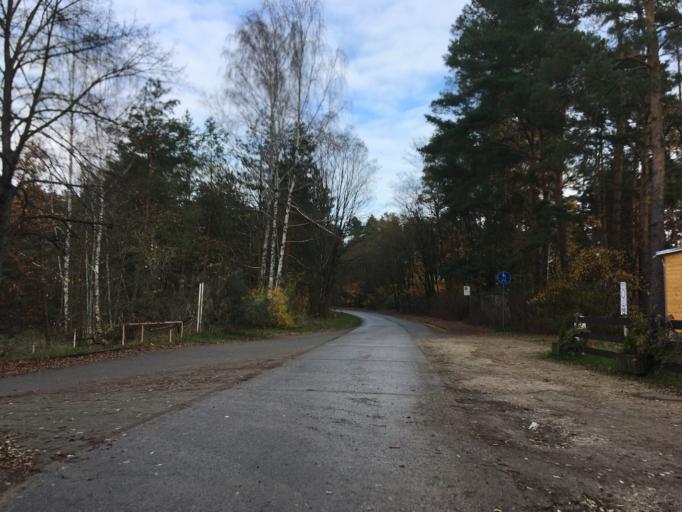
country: DE
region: Brandenburg
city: Schenkendobern
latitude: 51.9644
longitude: 14.5341
